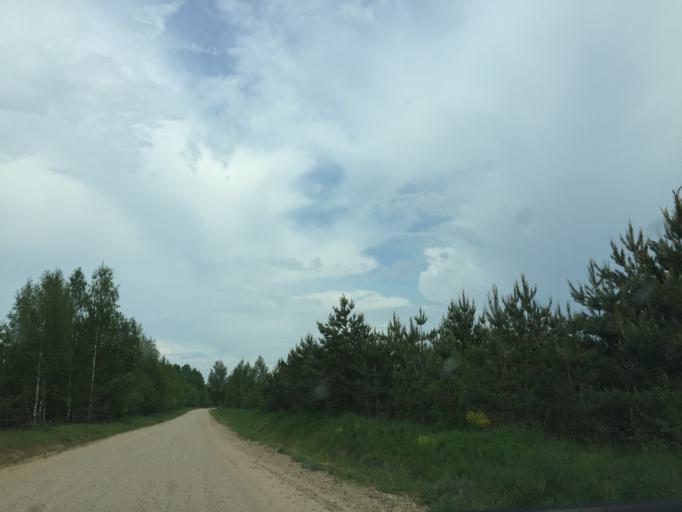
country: LV
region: Livani
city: Livani
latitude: 56.5626
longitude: 26.1315
